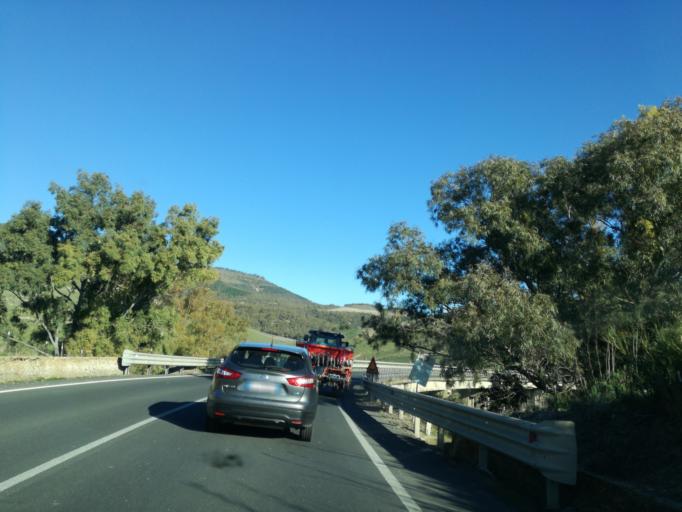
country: IT
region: Sicily
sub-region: Catania
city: San Michele di Ganzaria
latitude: 37.2378
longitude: 14.4500
